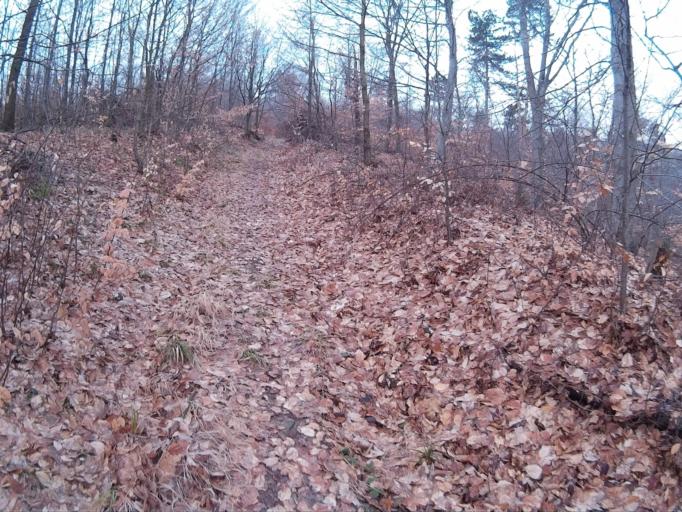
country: HU
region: Borsod-Abauj-Zemplen
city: Sarospatak
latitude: 48.3568
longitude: 21.5011
